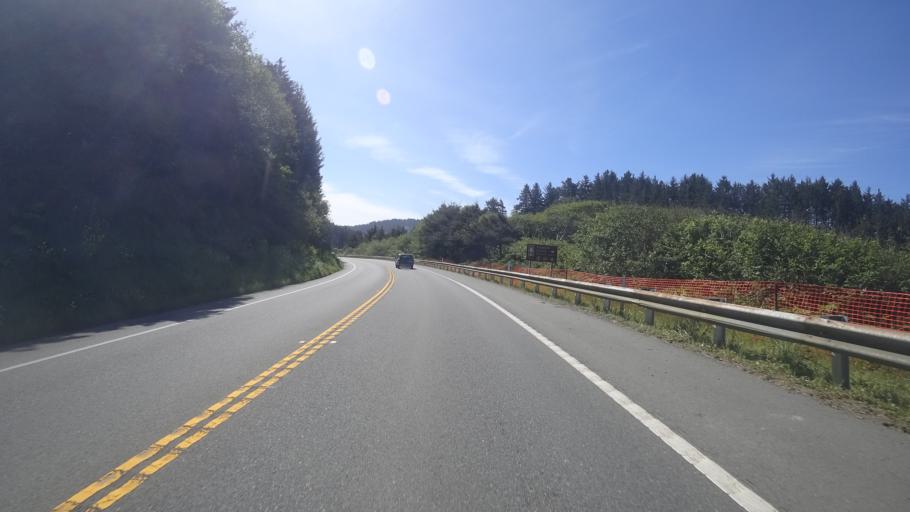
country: US
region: California
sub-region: Del Norte County
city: Bertsch-Oceanview
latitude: 41.5961
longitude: -124.1010
